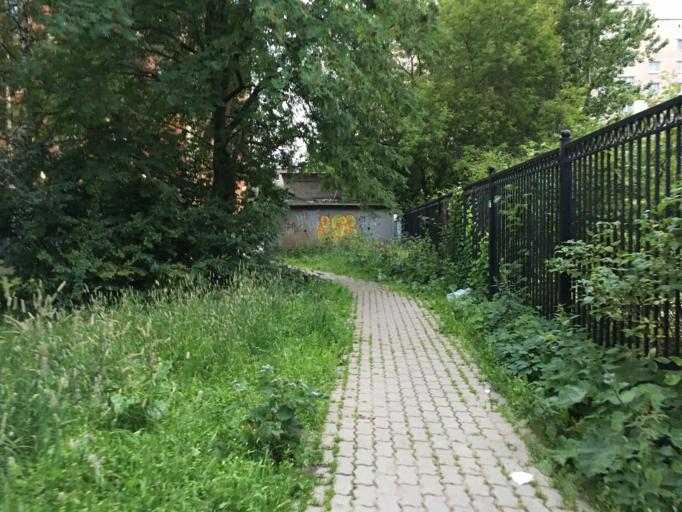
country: RU
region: St.-Petersburg
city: Vasyl'evsky Ostrov
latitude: 59.9354
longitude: 30.2459
